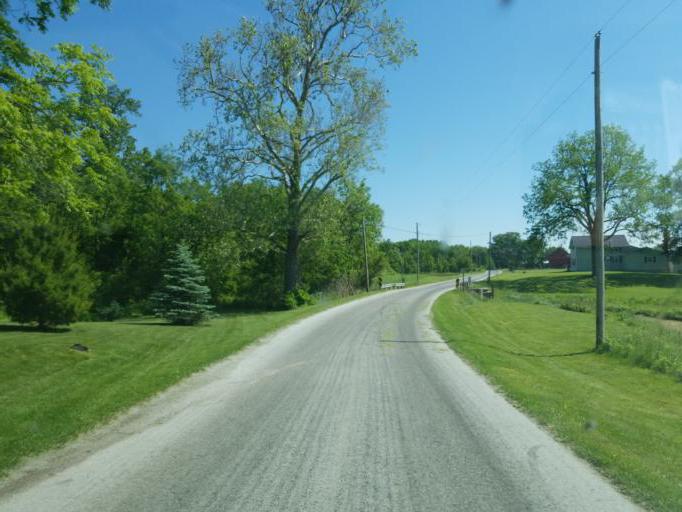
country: US
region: Ohio
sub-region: Hardin County
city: Kenton
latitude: 40.6076
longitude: -83.5127
